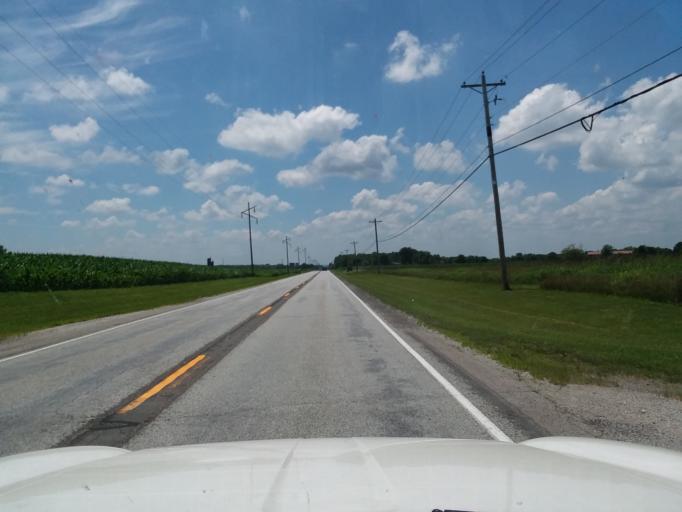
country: US
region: Indiana
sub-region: Johnson County
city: Trafalgar
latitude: 39.3958
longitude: -86.2058
